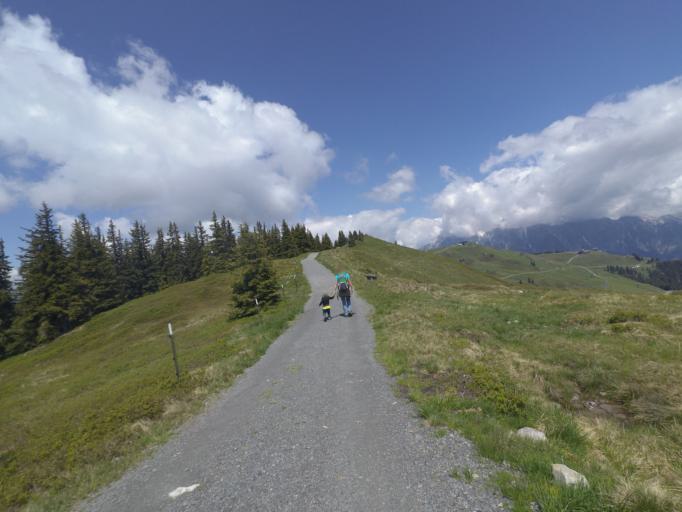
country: AT
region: Salzburg
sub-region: Politischer Bezirk Zell am See
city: Viehhofen
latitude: 47.3948
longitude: 12.7076
